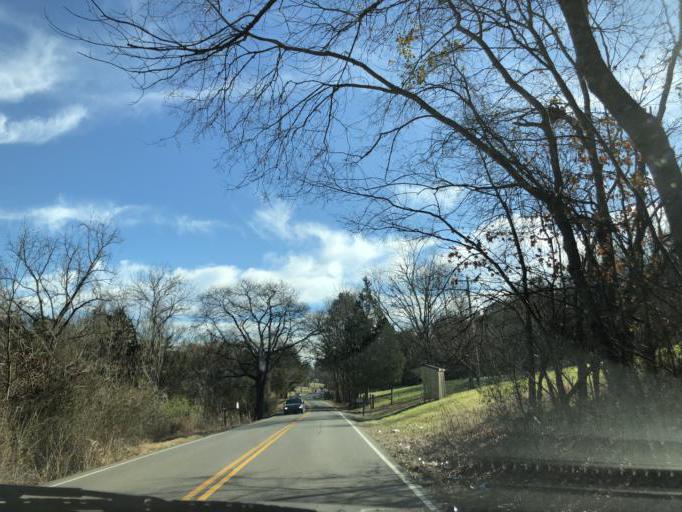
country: US
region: Tennessee
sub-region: Wilson County
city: Green Hill
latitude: 36.1720
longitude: -86.5658
